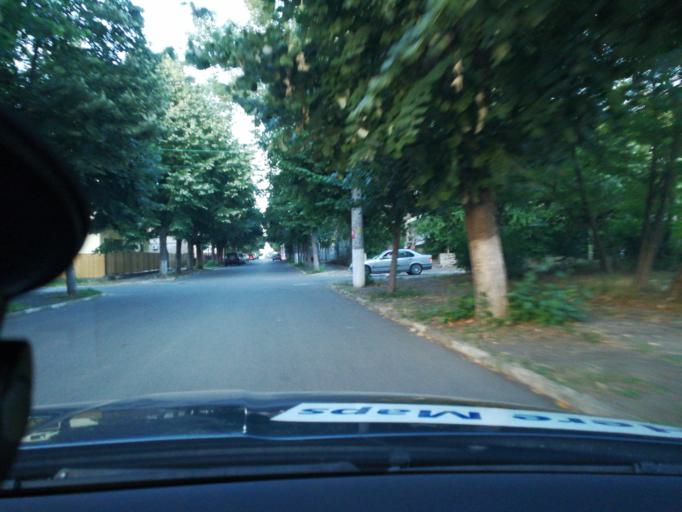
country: RO
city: Eforie Sud
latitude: 44.0257
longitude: 28.6524
